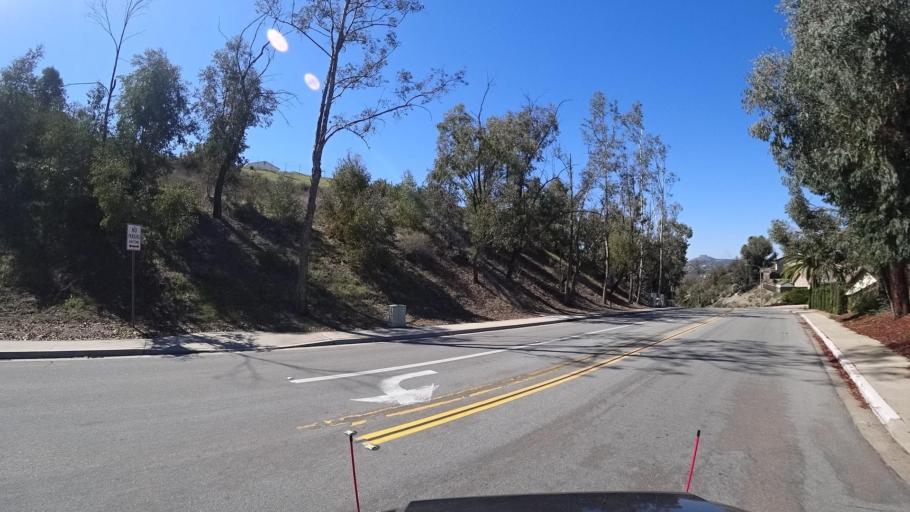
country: US
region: California
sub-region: San Diego County
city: Rancho San Diego
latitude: 32.7508
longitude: -116.9196
